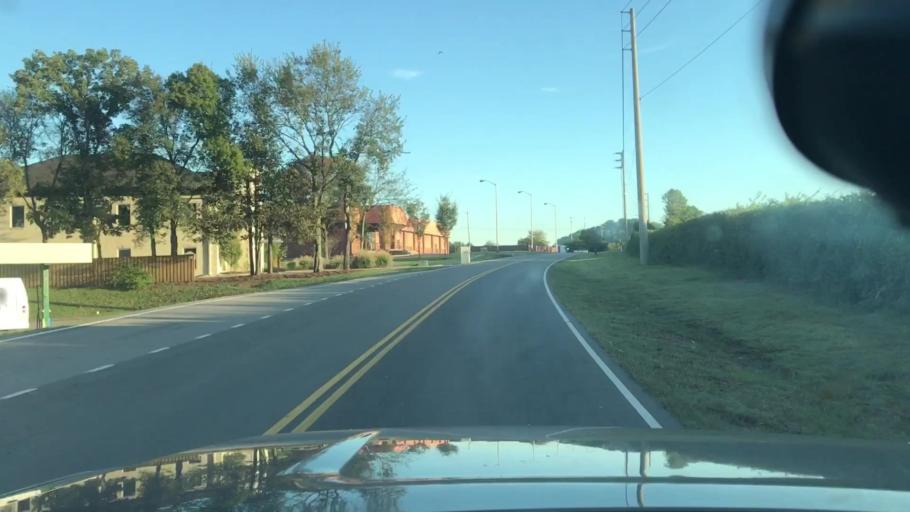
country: US
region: Tennessee
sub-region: Williamson County
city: Brentwood Estates
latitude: 36.0221
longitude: -86.7876
